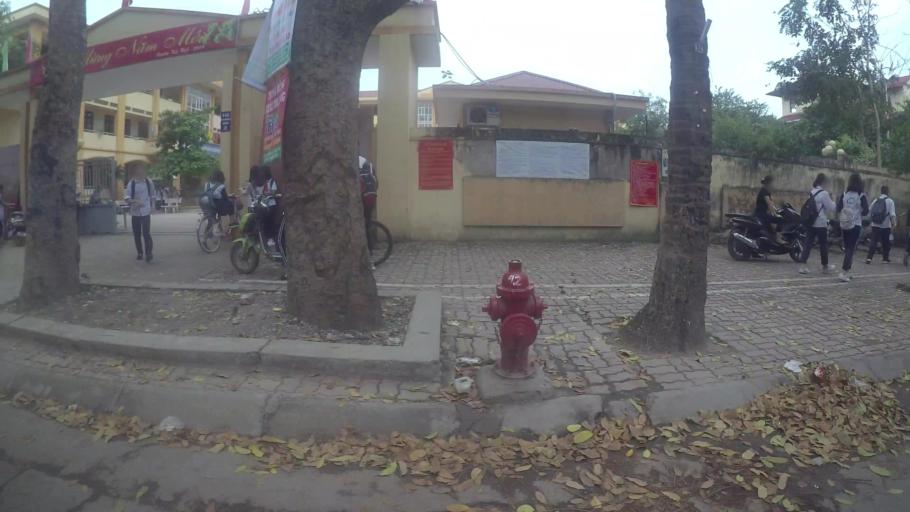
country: VN
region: Ha Noi
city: Tay Ho
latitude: 21.0714
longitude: 105.7954
